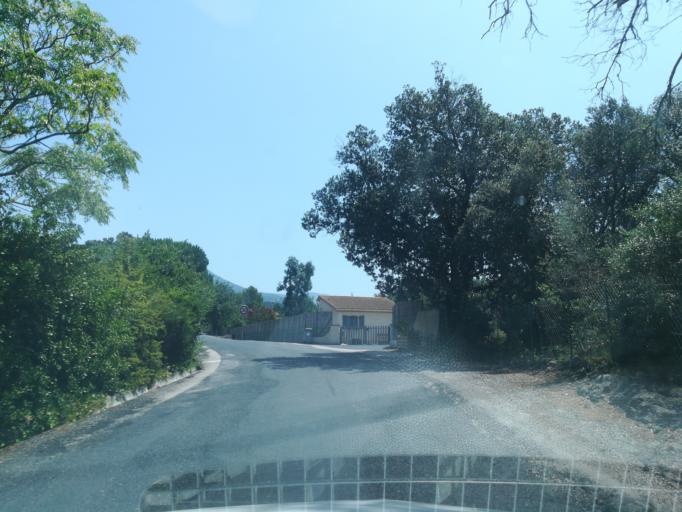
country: FR
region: Languedoc-Roussillon
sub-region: Departement des Pyrenees-Orientales
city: Maureillas-las-Illas
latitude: 42.4909
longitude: 2.8266
